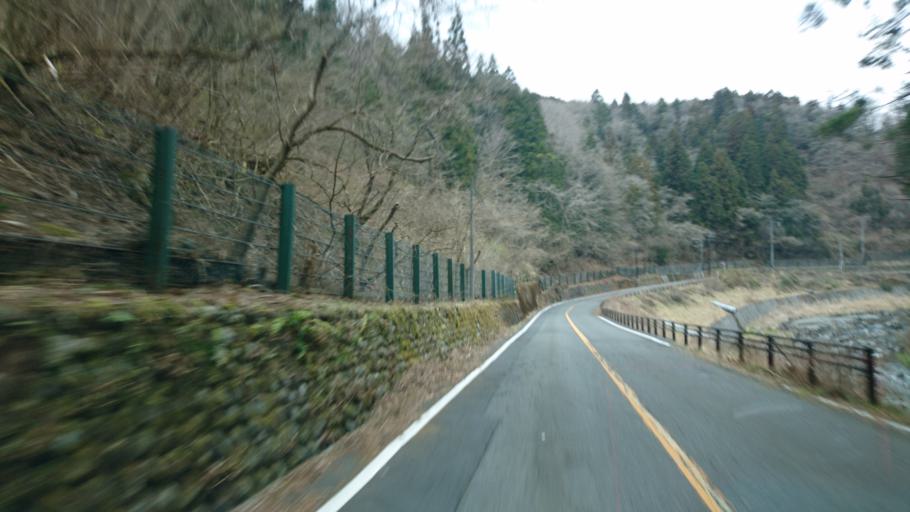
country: JP
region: Shizuoka
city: Fujinomiya
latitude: 35.3481
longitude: 138.5658
